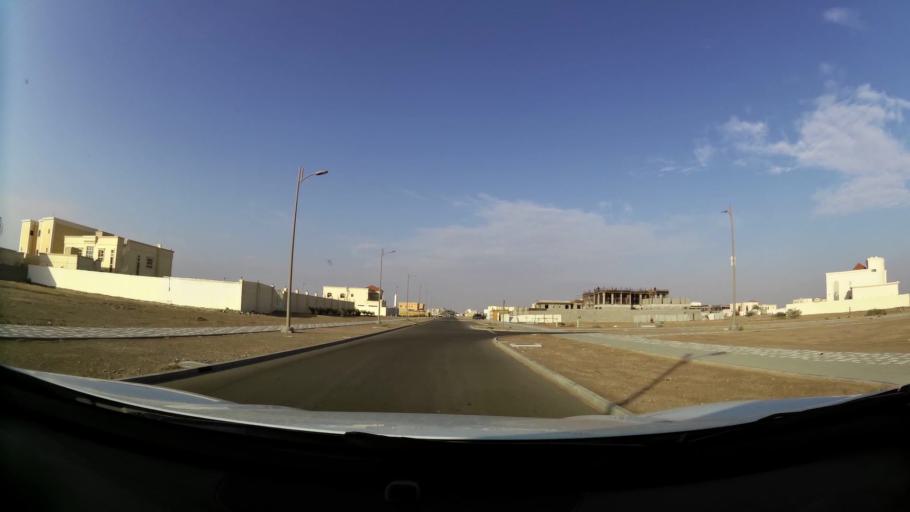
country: AE
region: Abu Dhabi
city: Al Ain
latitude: 24.1044
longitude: 55.8469
